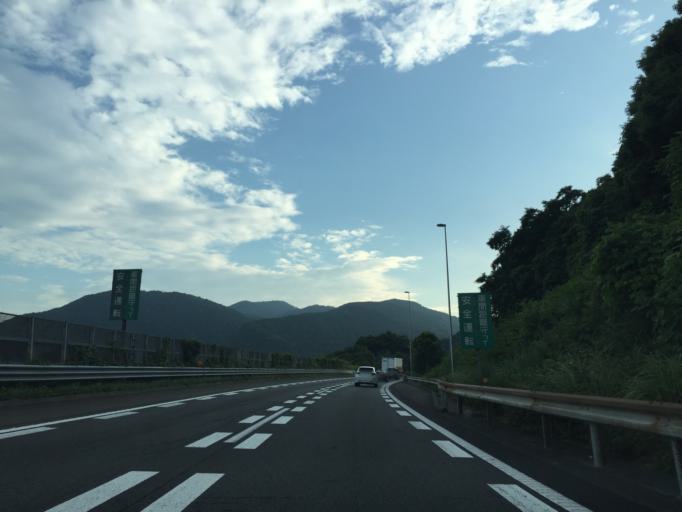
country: JP
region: Kanagawa
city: Odawara
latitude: 35.3634
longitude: 139.0778
